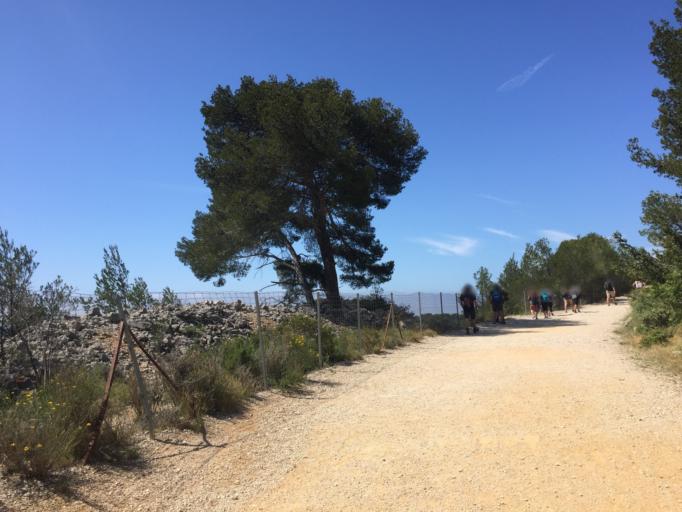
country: FR
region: Provence-Alpes-Cote d'Azur
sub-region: Departement des Bouches-du-Rhone
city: Cassis
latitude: 43.2061
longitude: 5.5141
